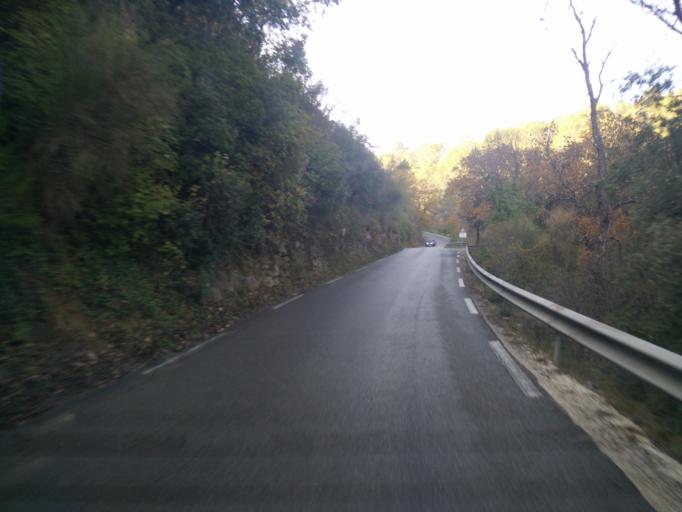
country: FR
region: Provence-Alpes-Cote d'Azur
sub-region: Departement du Var
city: Sollies-Toucas
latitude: 43.2035
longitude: 6.0119
